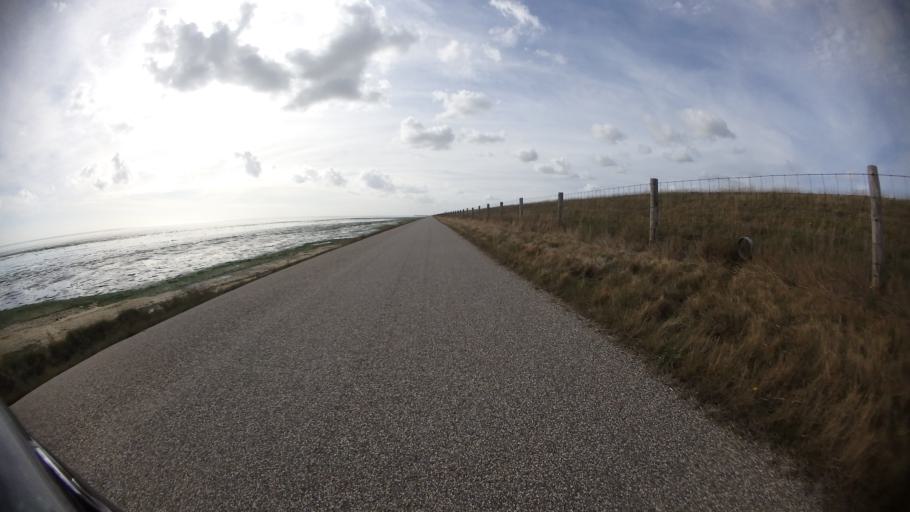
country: NL
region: North Holland
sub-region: Gemeente Texel
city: Den Burg
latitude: 53.1218
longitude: 4.8993
